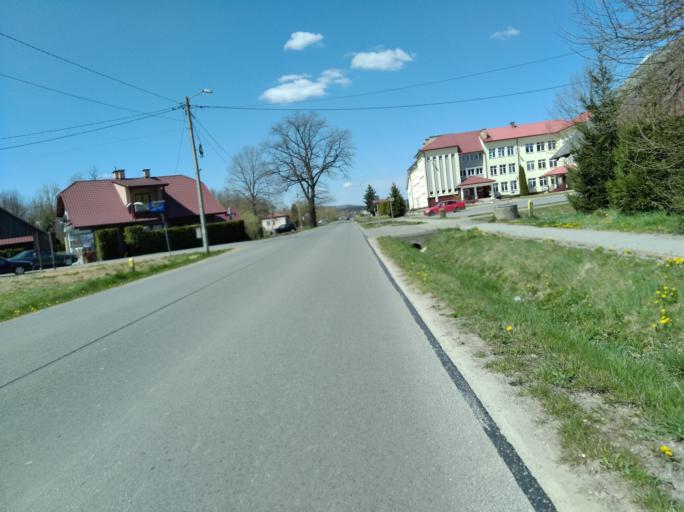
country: PL
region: Subcarpathian Voivodeship
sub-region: Powiat brzozowski
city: Dydnia
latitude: 49.6846
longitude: 22.1759
